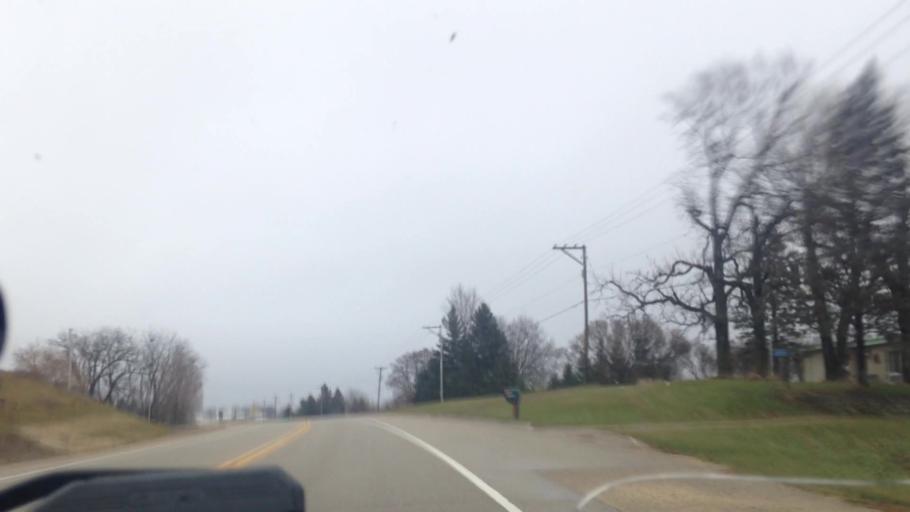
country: US
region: Wisconsin
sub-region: Dodge County
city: Beaver Dam
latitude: 43.4447
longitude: -88.7751
